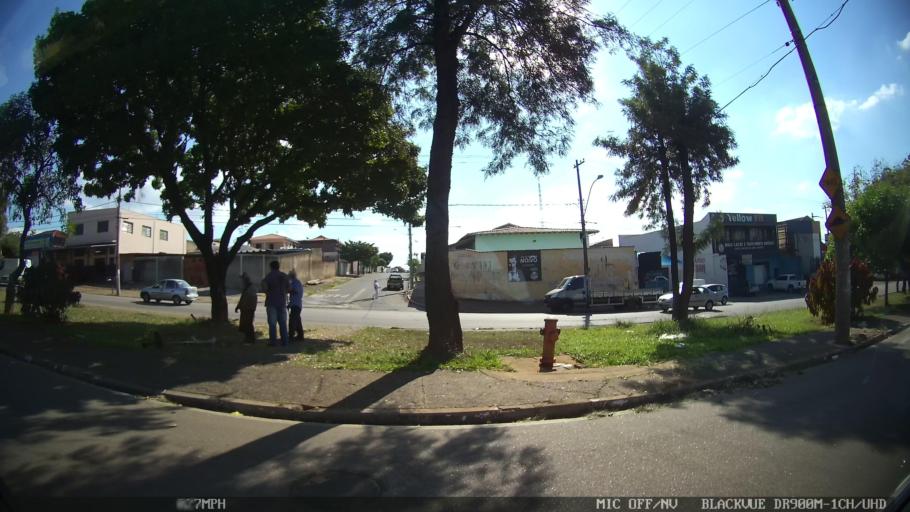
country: BR
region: Sao Paulo
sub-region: Sumare
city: Sumare
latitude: -22.8105
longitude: -47.2824
